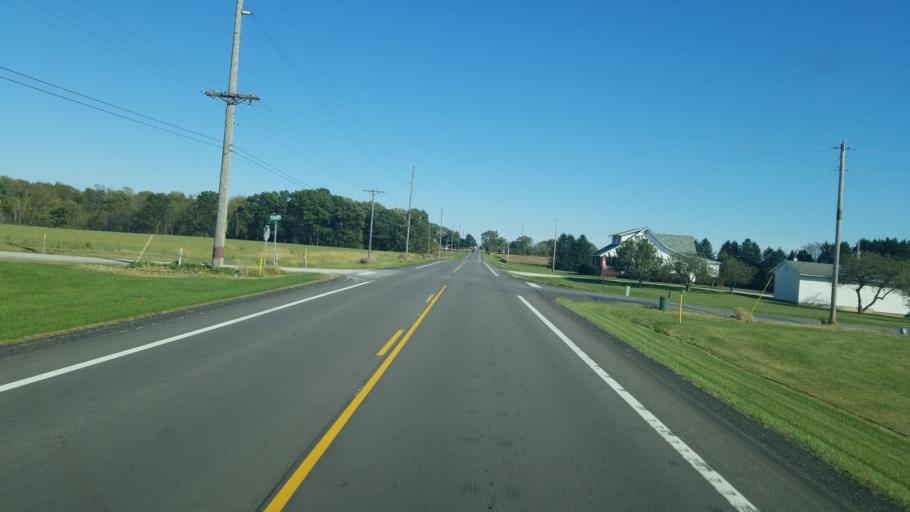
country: US
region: Ohio
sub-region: Wayne County
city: West Salem
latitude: 41.0274
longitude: -82.1473
